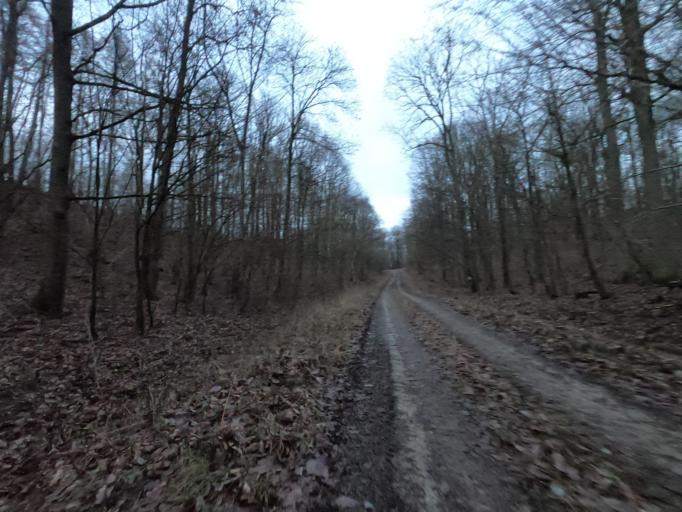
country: PL
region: Greater Poland Voivodeship
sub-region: Powiat pilski
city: Wyrzysk
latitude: 53.1226
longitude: 17.2208
